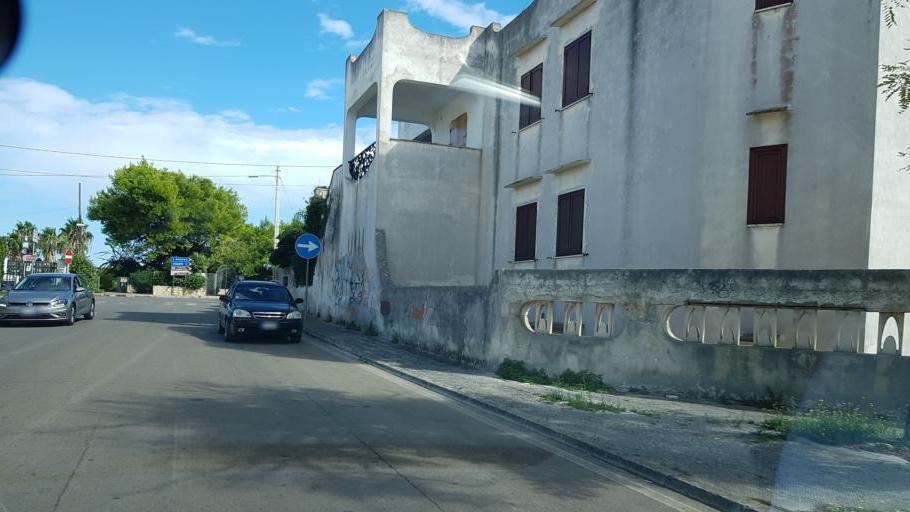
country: IT
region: Apulia
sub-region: Provincia di Lecce
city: Borgagne
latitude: 40.2710
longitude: 18.4281
